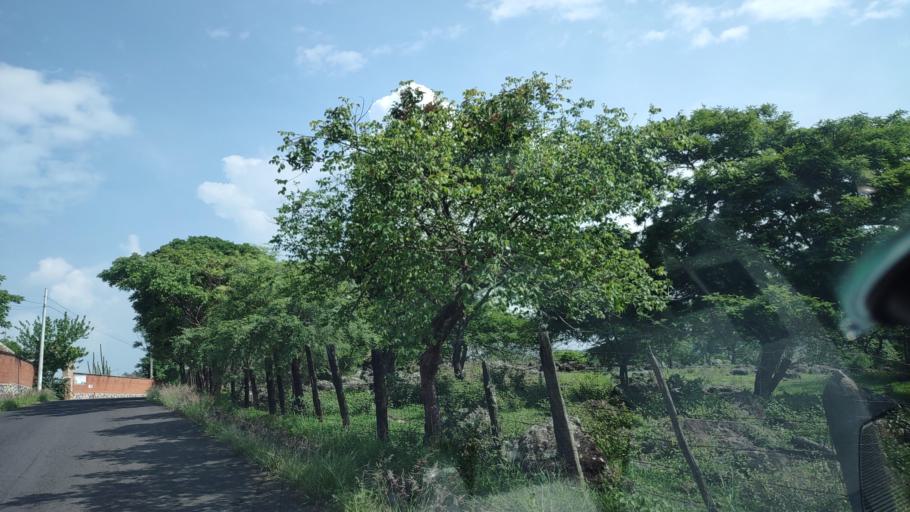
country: MX
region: Veracruz
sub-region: Coatepec
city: Bella Esperanza
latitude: 19.4530
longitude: -96.8310
